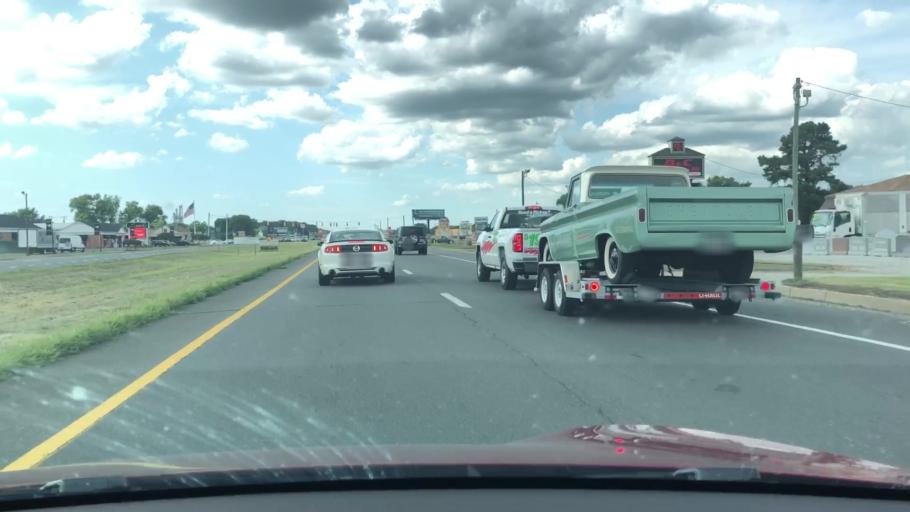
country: US
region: Delaware
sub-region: Sussex County
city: Laurel
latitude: 38.5633
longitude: -75.5582
